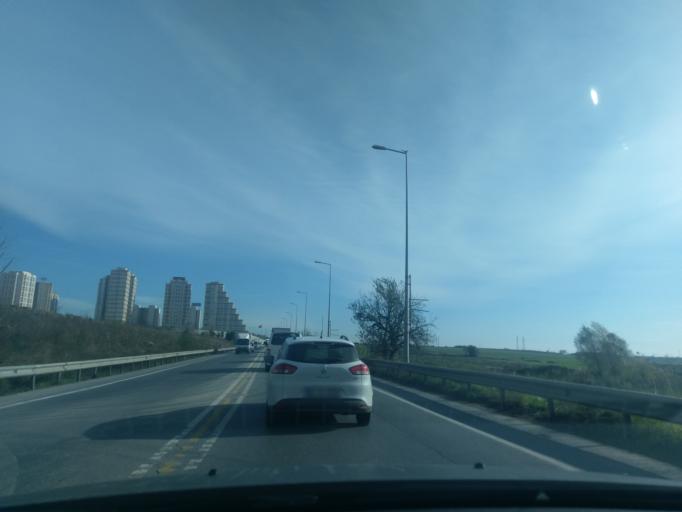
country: TR
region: Istanbul
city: Esenyurt
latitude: 41.0562
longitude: 28.7070
